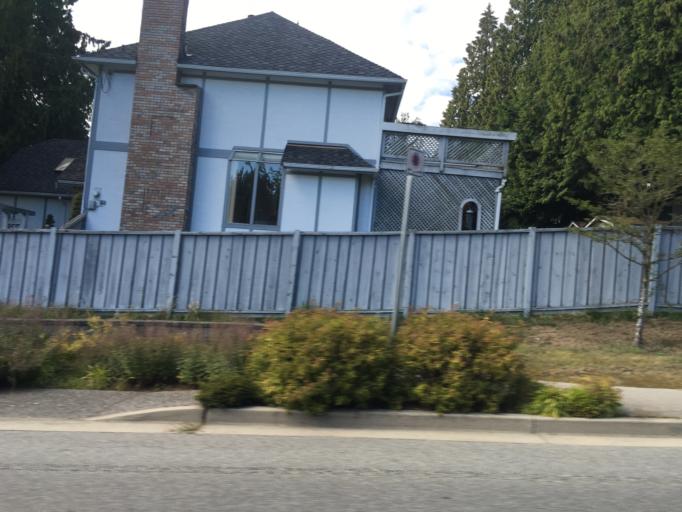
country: CA
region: British Columbia
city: Port Moody
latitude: 49.2454
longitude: -122.8795
